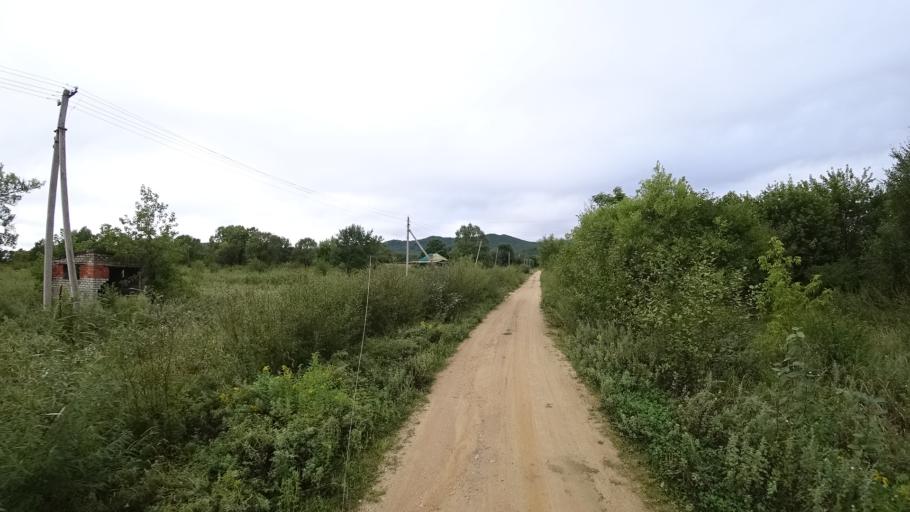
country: RU
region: Primorskiy
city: Rettikhovka
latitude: 44.1374
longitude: 132.6378
